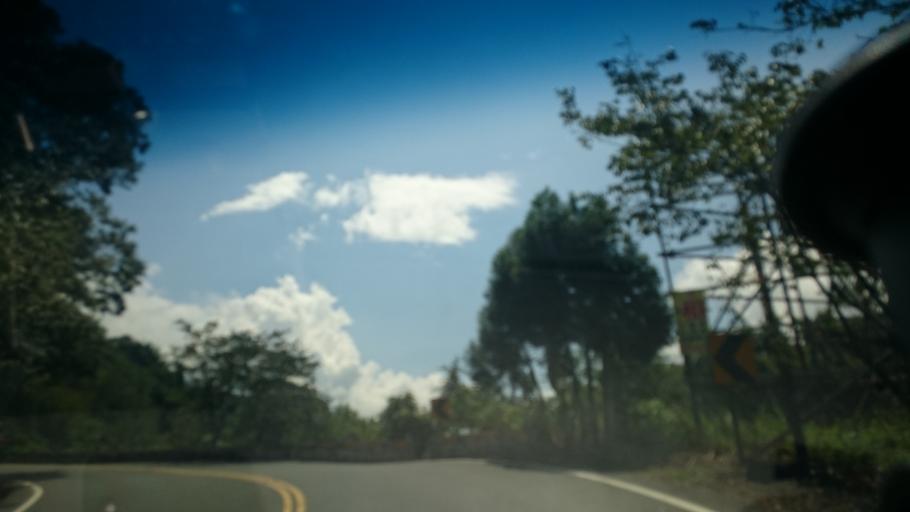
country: TW
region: Taiwan
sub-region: Nantou
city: Puli
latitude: 24.0162
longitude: 121.1270
